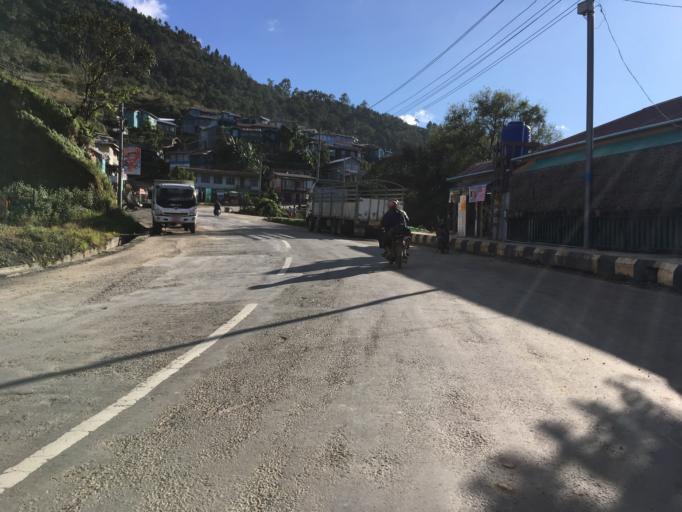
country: MM
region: Chin
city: Hakha
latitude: 22.6404
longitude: 93.6131
